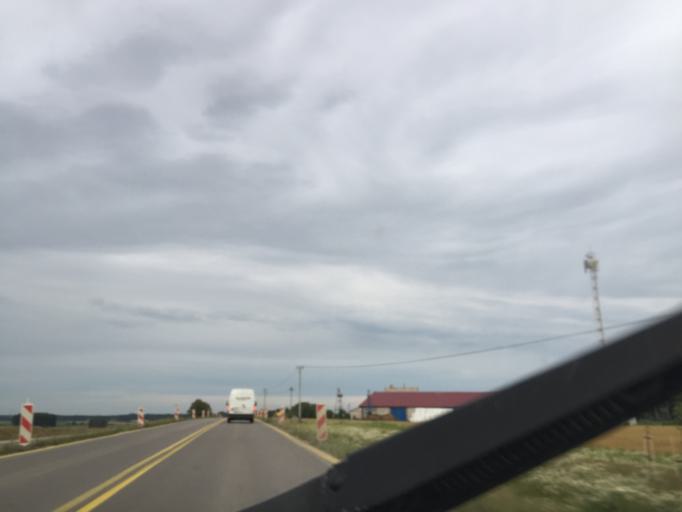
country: PL
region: Podlasie
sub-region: Powiat wysokomazowiecki
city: Sokoly
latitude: 53.1180
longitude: 22.6385
